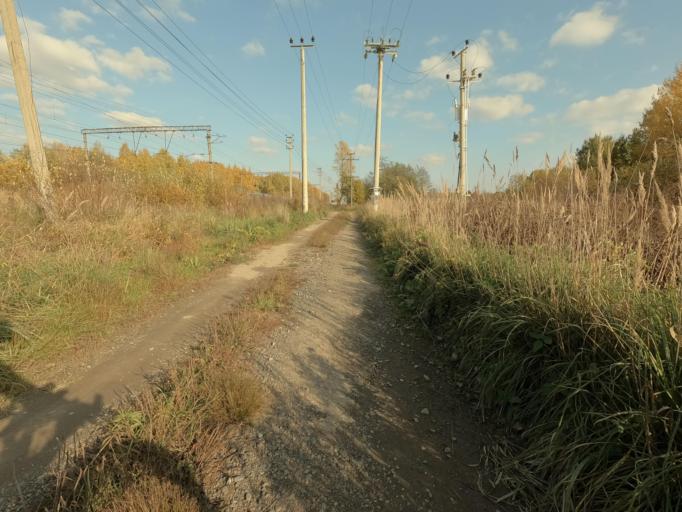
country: RU
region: Leningrad
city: Mga
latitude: 59.7574
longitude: 31.1105
